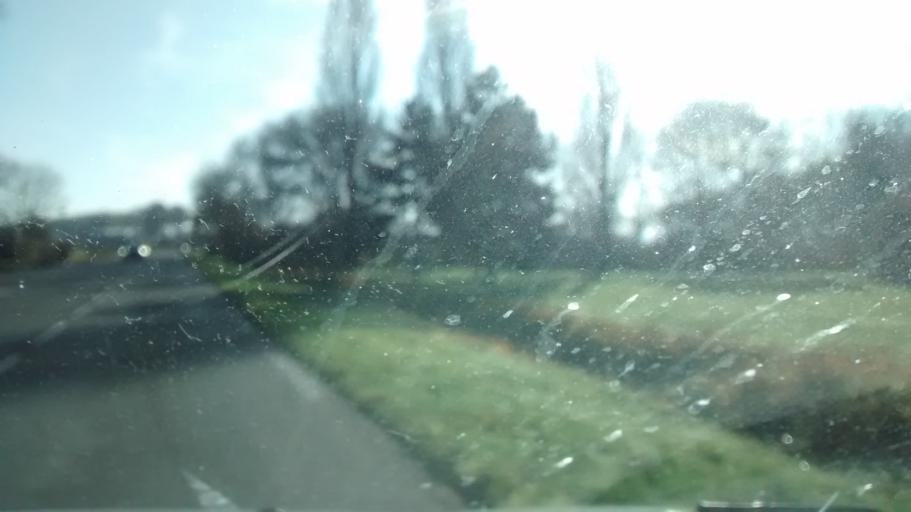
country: FR
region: Centre
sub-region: Departement d'Indre-et-Loire
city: Nazelles-Negron
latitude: 47.4294
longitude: 0.9566
